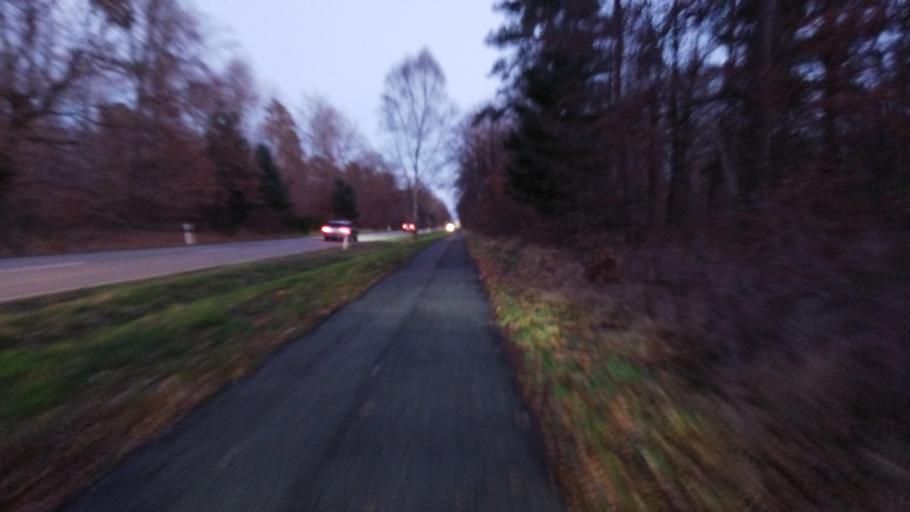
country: DE
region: Rheinland-Pfalz
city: Dudenhofen
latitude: 49.3416
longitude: 8.3940
